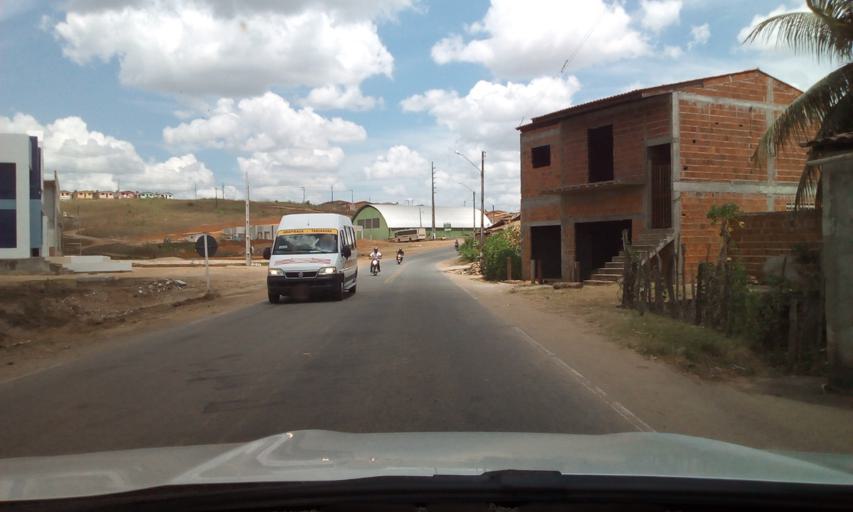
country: BR
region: Paraiba
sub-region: Guarabira
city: Guarabira
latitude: -6.8950
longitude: -35.5245
